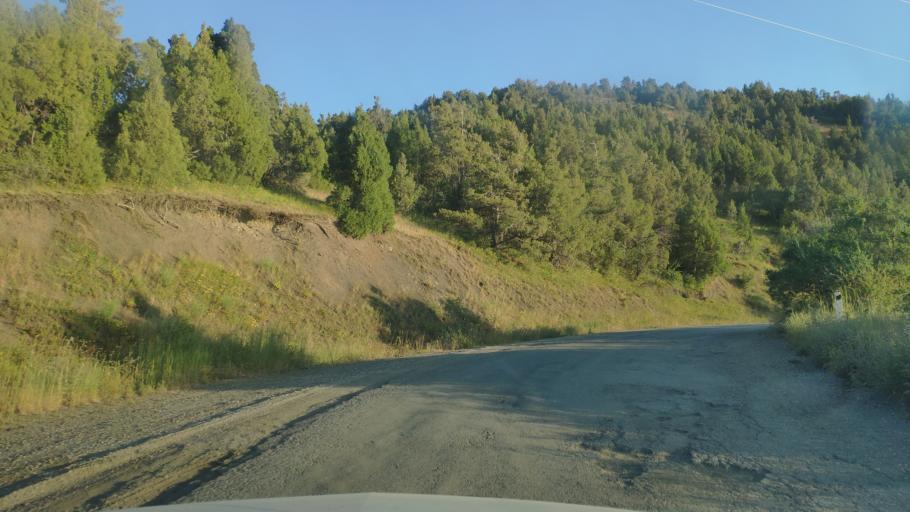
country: TJ
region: Viloyati Sughd
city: Ayni
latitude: 39.6400
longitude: 68.4702
